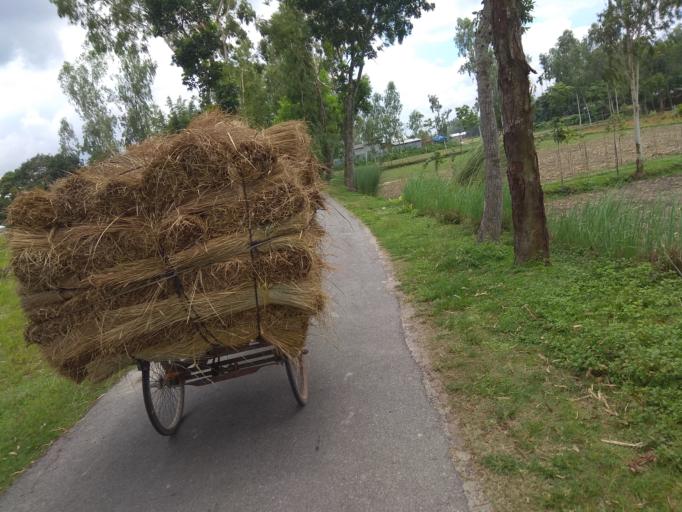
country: IN
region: West Bengal
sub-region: Koch Bihar
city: Haldibari
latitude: 26.2417
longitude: 88.8922
